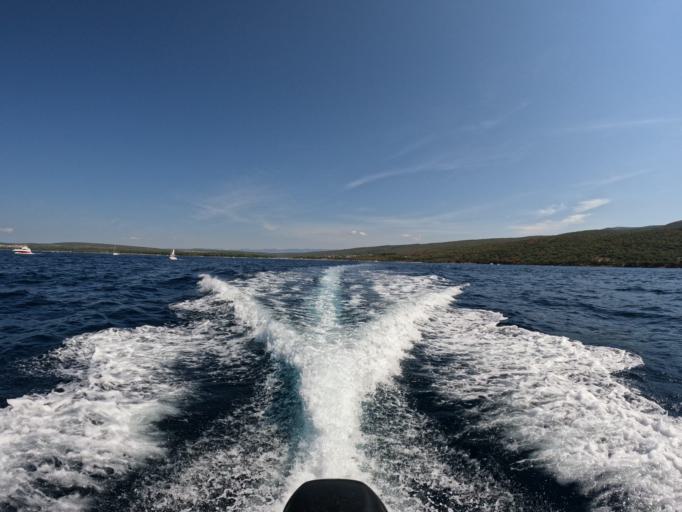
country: HR
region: Primorsko-Goranska
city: Punat
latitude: 44.9948
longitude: 14.6173
